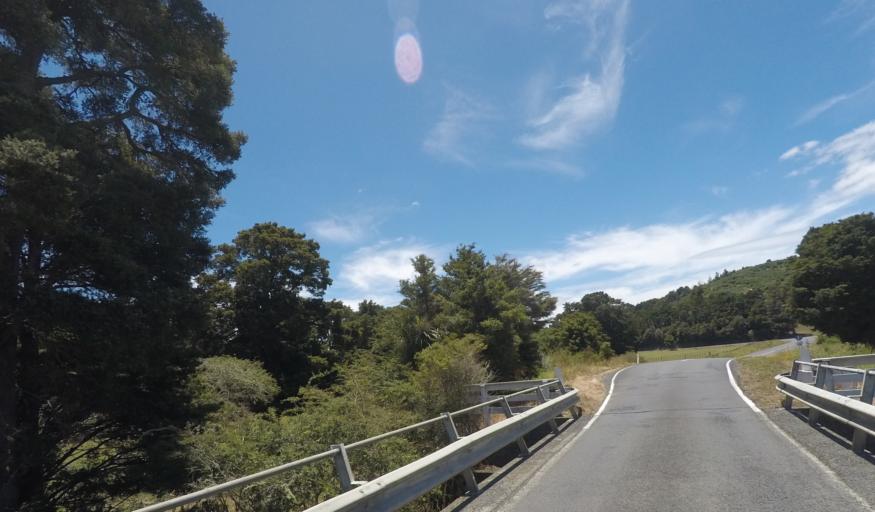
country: NZ
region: Northland
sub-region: Whangarei
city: Whangarei
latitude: -35.5421
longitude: 174.3088
